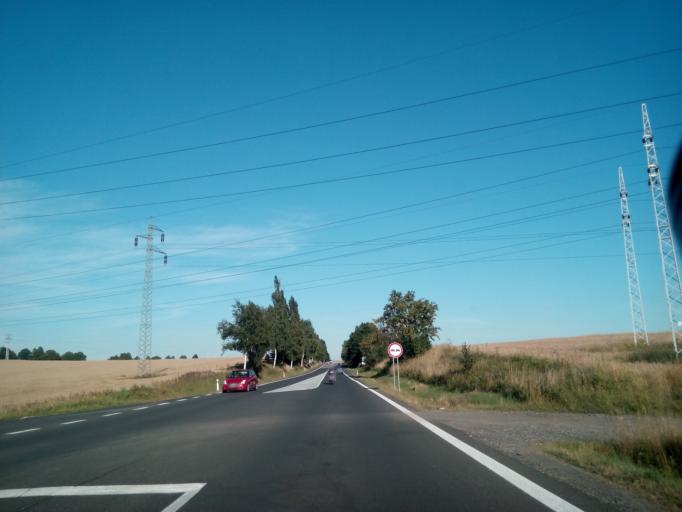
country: SK
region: Presovsky
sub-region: Okres Poprad
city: Poprad
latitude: 49.0492
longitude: 20.3114
